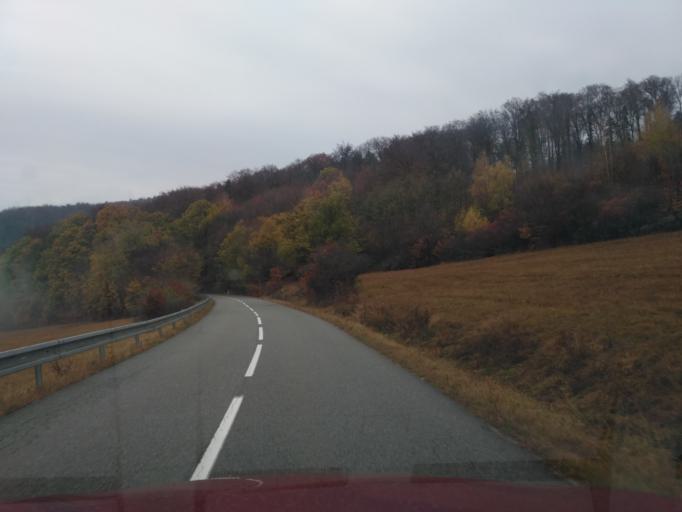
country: SK
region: Kosicky
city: Medzev
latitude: 48.7140
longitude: 20.8051
